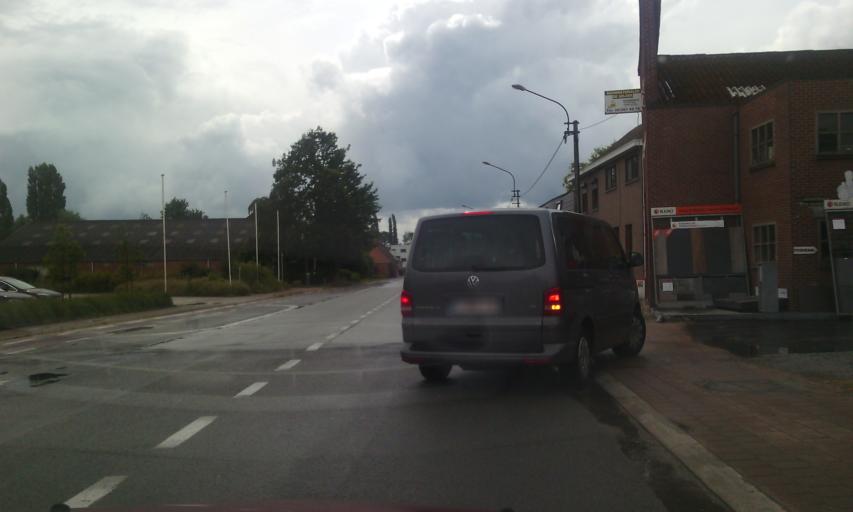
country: BE
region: Flanders
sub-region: Provincie Oost-Vlaanderen
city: Wetteren
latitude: 51.0336
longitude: 3.9115
